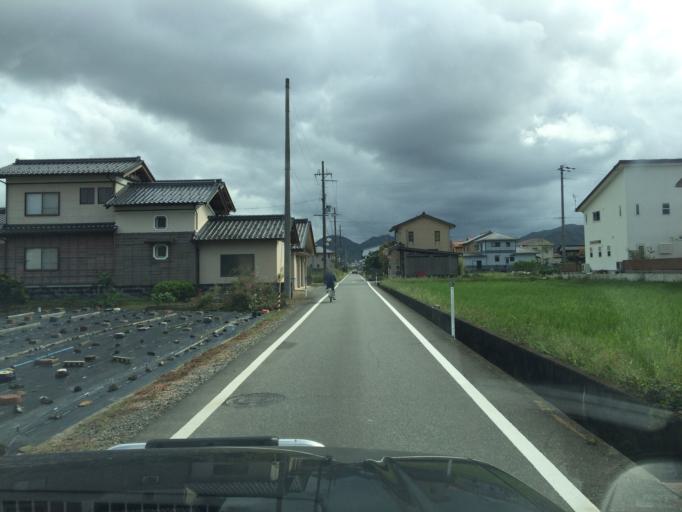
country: JP
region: Hyogo
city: Toyooka
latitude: 35.4758
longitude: 134.7775
